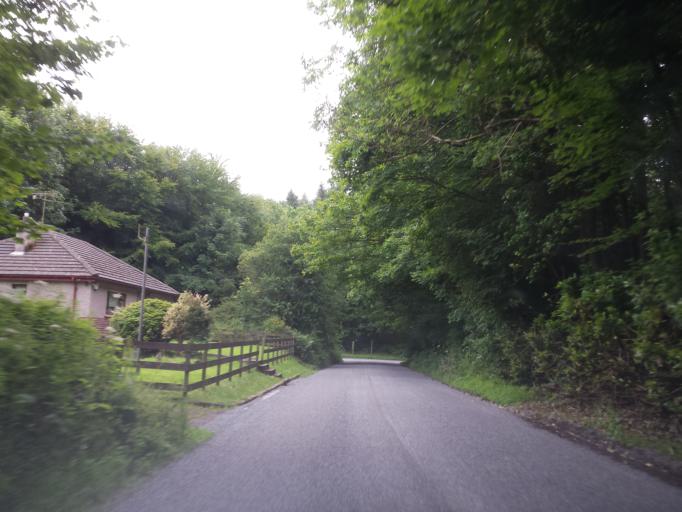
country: GB
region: Scotland
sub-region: Dumfries and Galloway
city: Stranraer
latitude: 54.8500
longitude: -5.1061
